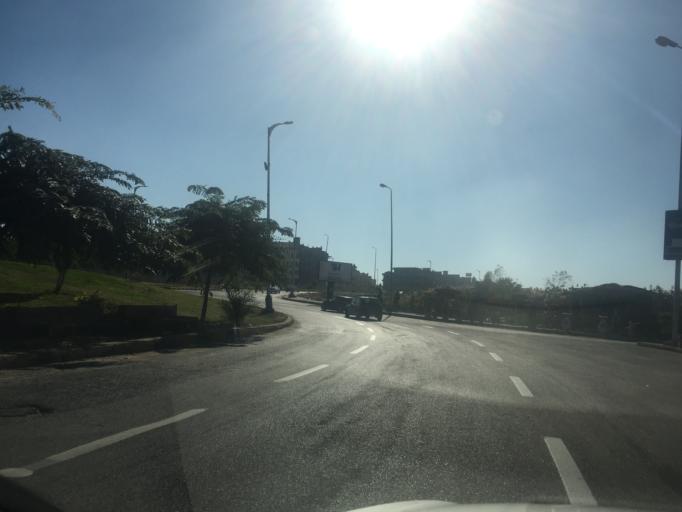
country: EG
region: Al Jizah
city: Awsim
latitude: 30.0214
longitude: 30.9812
